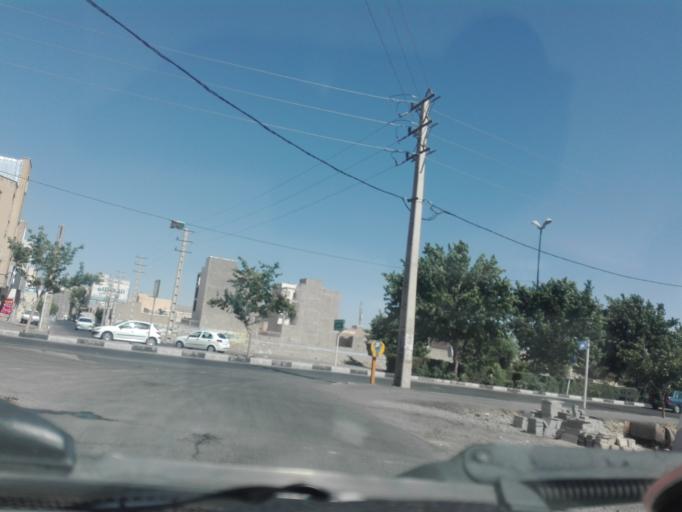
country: IR
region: Tehran
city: Malard
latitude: 35.7193
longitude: 50.9790
